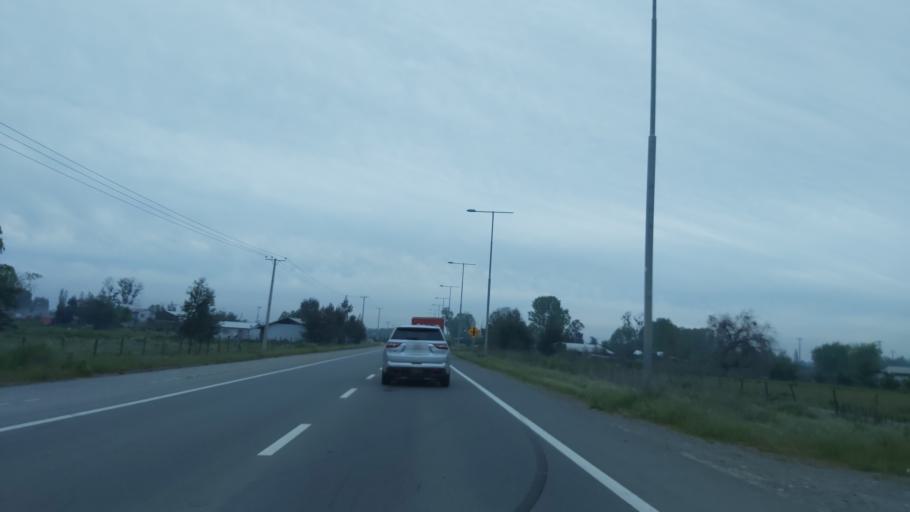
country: CL
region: Maule
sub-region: Provincia de Linares
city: Linares
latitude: -35.8293
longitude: -71.6112
